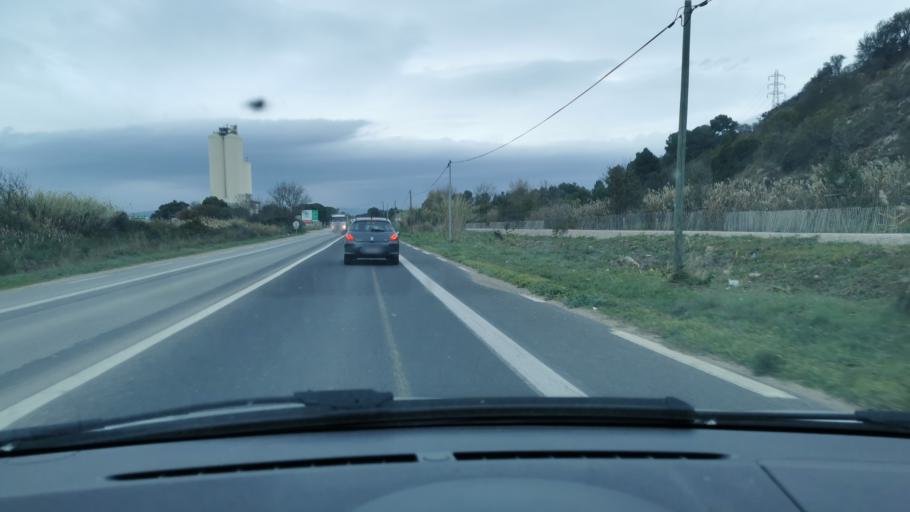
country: FR
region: Languedoc-Roussillon
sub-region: Departement de l'Herault
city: Sete
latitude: 43.4268
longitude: 3.7070
